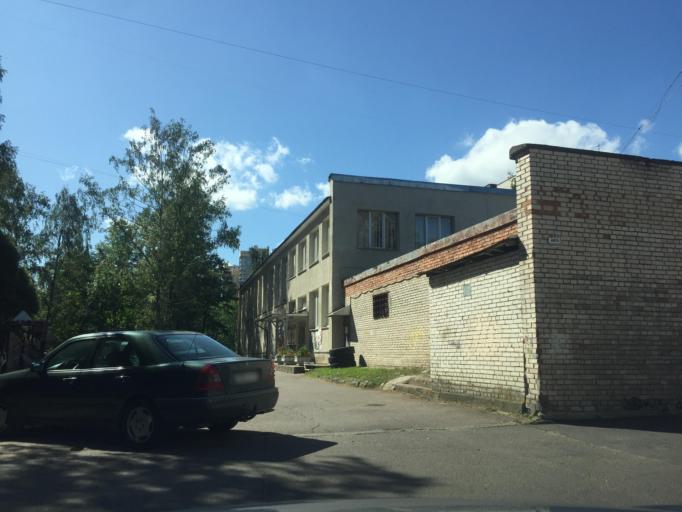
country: RU
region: Leningrad
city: Akademicheskoe
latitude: 60.0082
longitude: 30.4082
